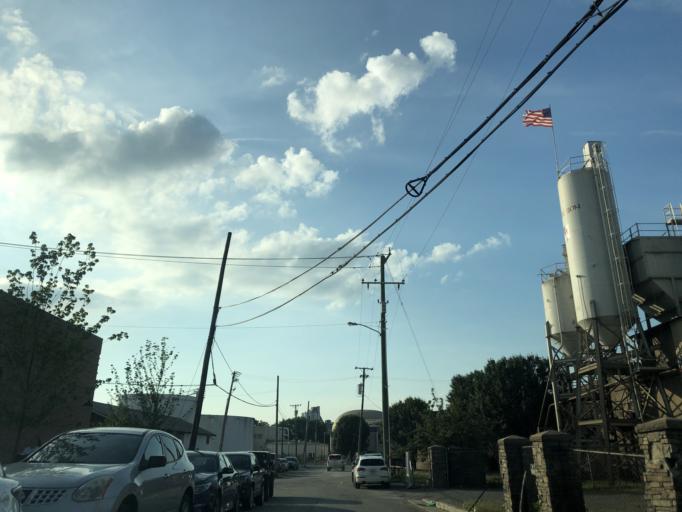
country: US
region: Tennessee
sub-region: Davidson County
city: Nashville
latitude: 36.1818
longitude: -86.7846
